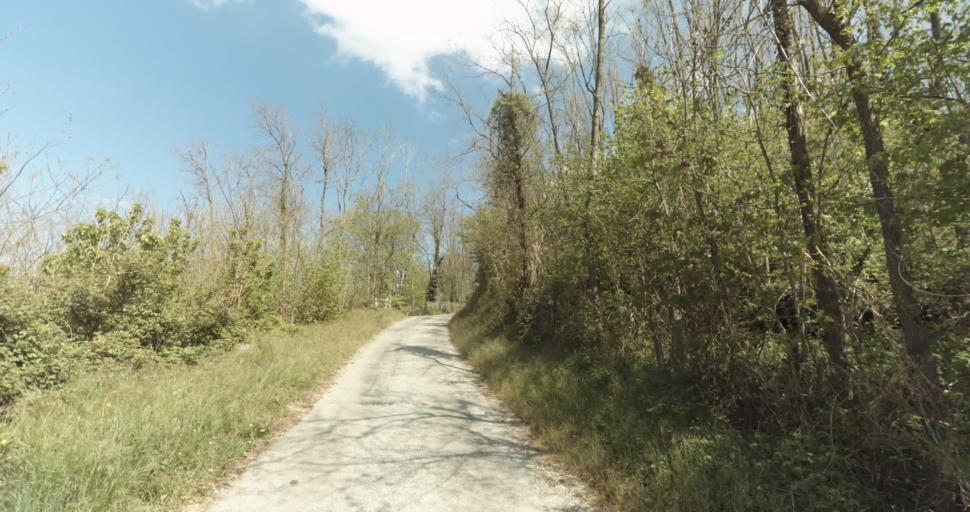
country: FR
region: Rhone-Alpes
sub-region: Departement de l'Isere
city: Chatte
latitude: 45.1550
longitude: 5.3008
